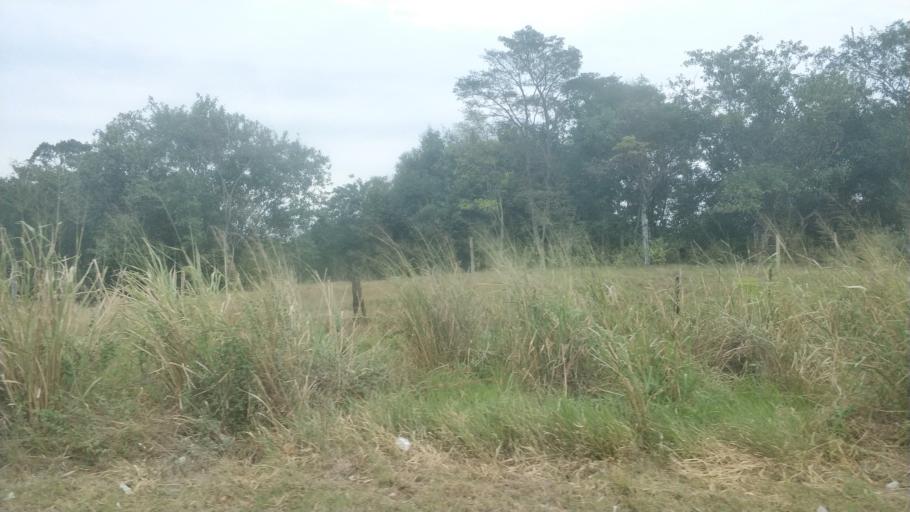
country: BR
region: Rio de Janeiro
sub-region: Seropedica
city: Seropedica
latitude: -22.7749
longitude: -43.6654
